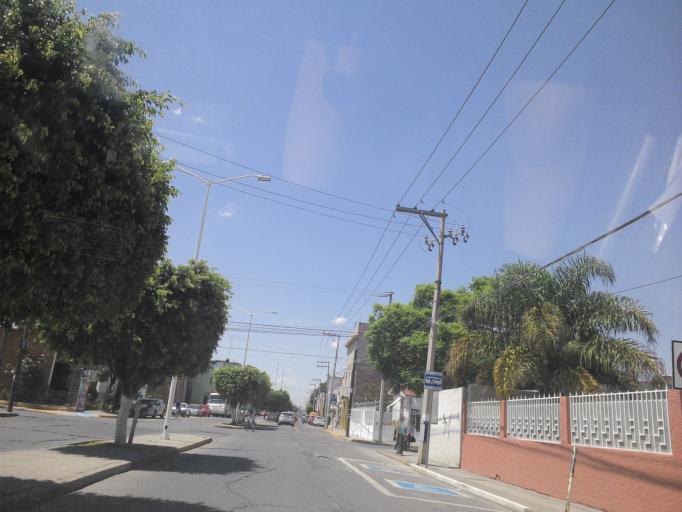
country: MX
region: Guanajuato
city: San Francisco del Rincon
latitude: 21.0138
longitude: -101.8591
